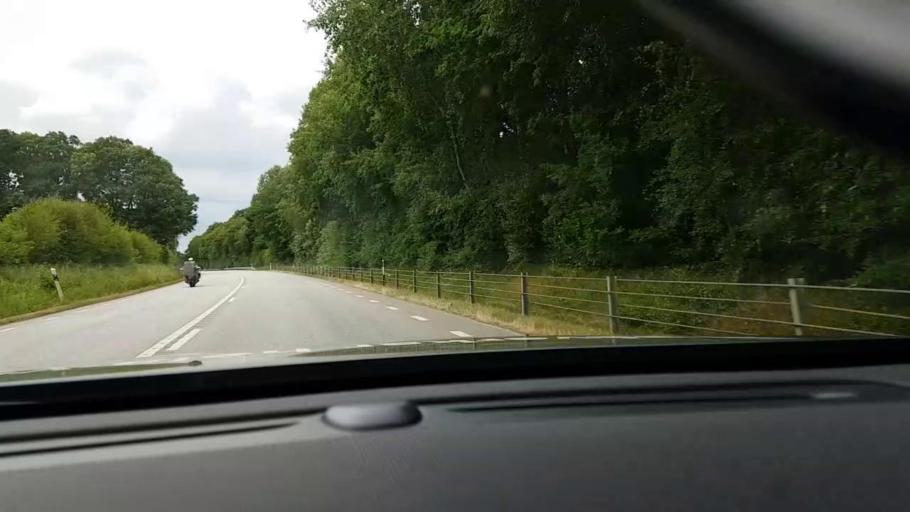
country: SE
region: Skane
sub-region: Horby Kommun
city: Hoerby
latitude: 55.8683
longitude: 13.6376
